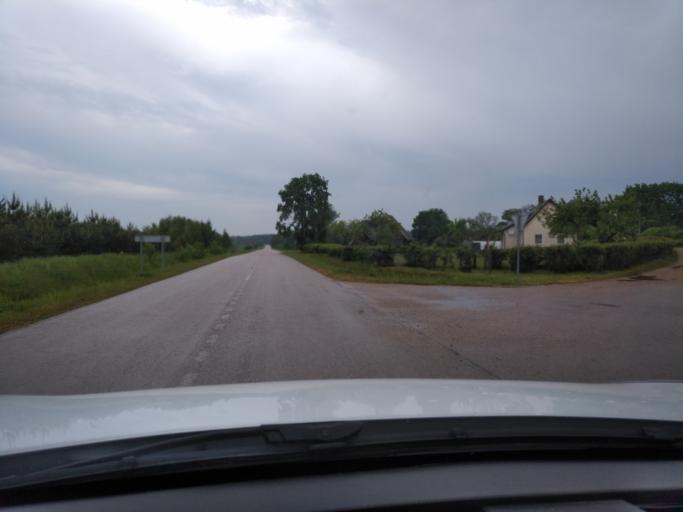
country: LT
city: Svencionys
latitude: 55.1830
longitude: 26.1405
